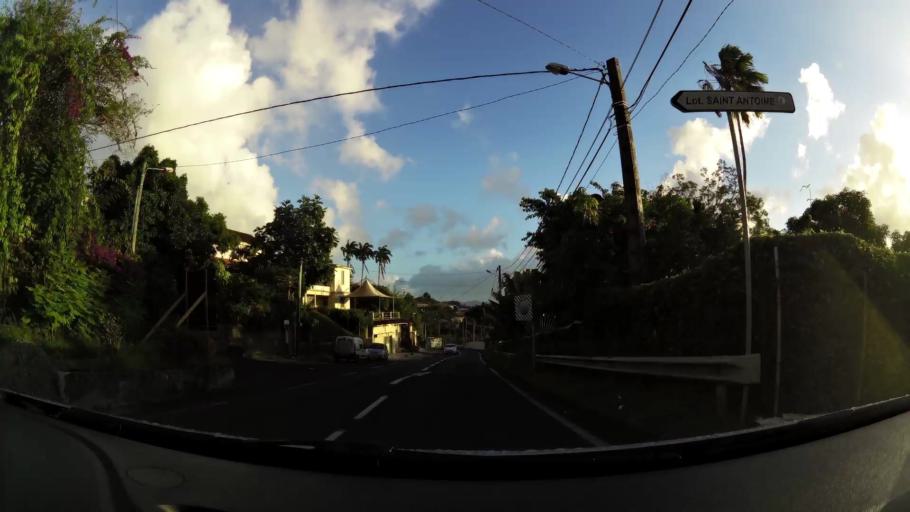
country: MQ
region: Martinique
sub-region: Martinique
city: Fort-de-France
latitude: 14.6267
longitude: -61.0729
